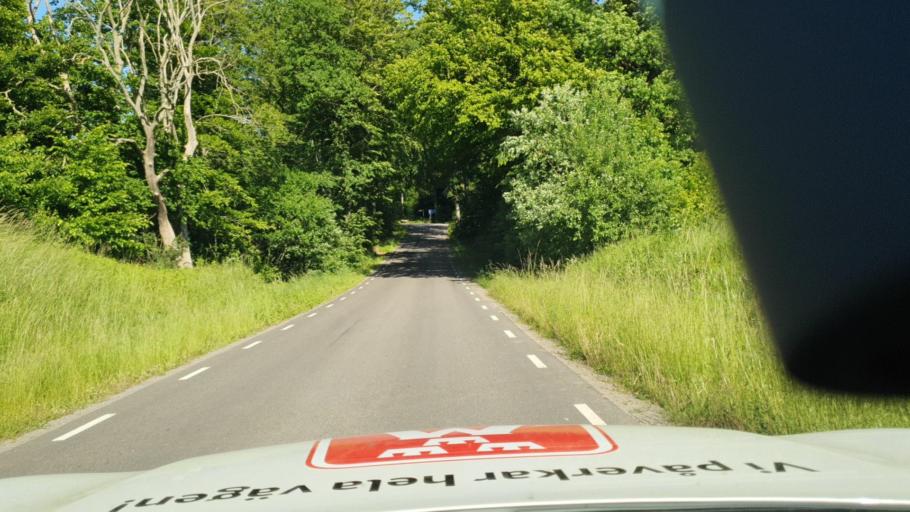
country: SE
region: Skane
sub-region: Sjobo Kommun
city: Sjoebo
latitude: 55.6505
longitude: 13.7568
